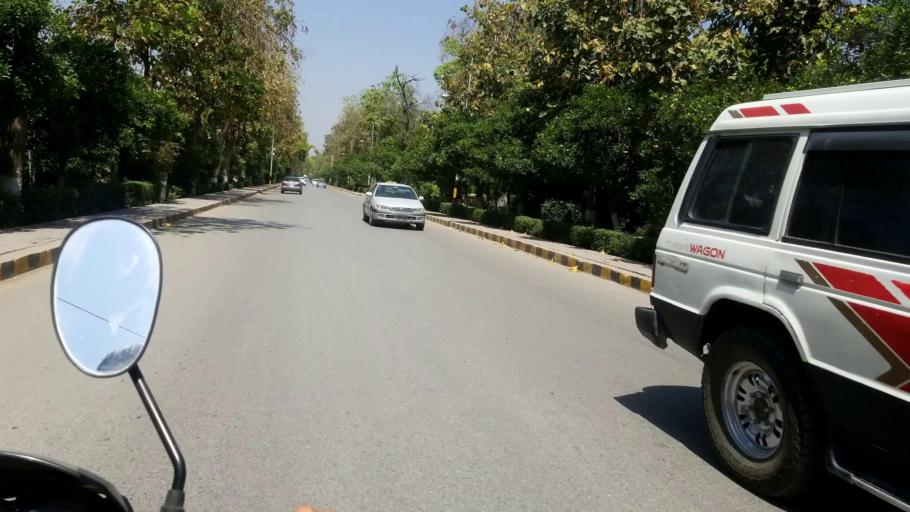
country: PK
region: Khyber Pakhtunkhwa
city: Peshawar
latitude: 34.0020
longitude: 71.4863
